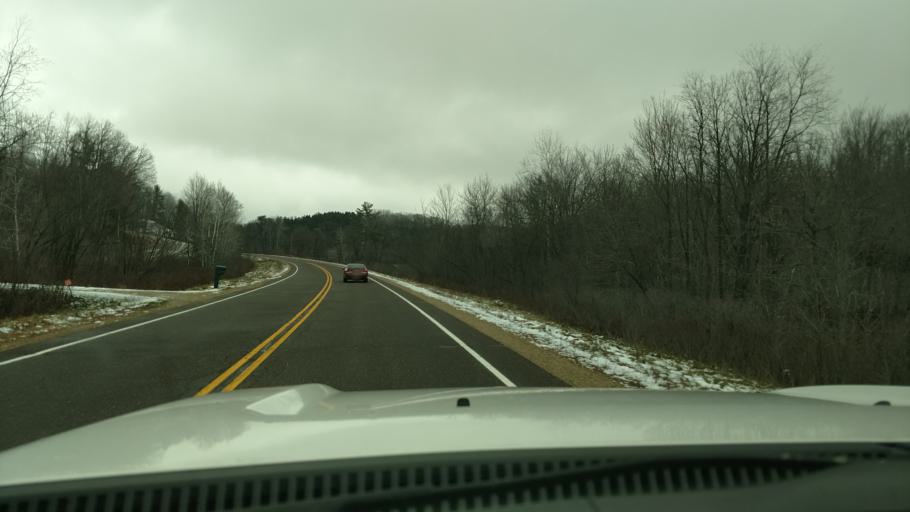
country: US
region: Wisconsin
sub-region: Dunn County
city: Boyceville
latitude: 45.1301
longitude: -91.9959
